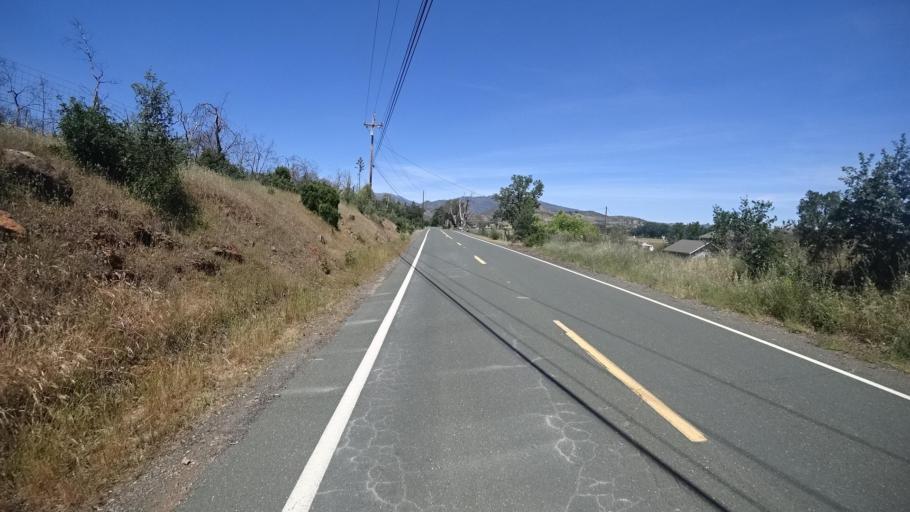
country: US
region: California
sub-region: Lake County
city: Middletown
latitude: 38.7540
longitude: -122.6012
